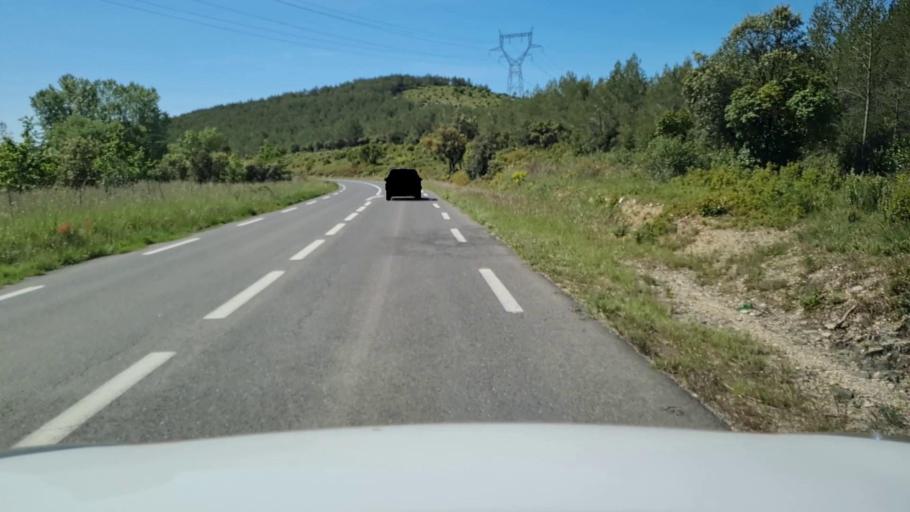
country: FR
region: Languedoc-Roussillon
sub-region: Departement du Gard
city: Villevieille
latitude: 43.8515
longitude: 4.0957
